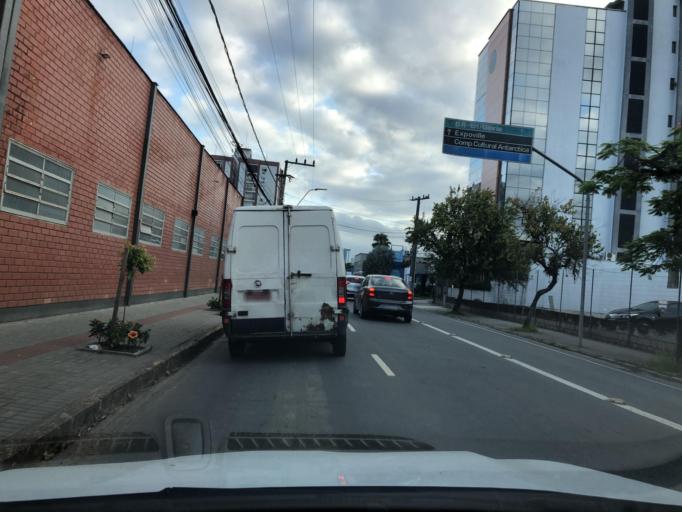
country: BR
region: Santa Catarina
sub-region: Joinville
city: Joinville
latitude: -26.2914
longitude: -48.8499
